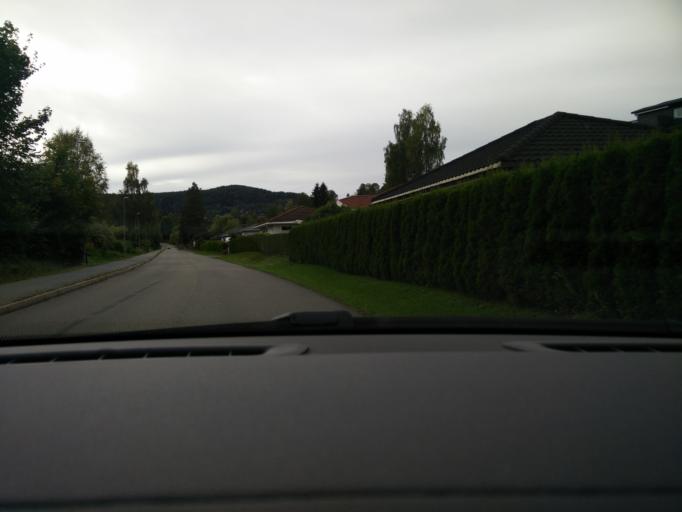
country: NO
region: Akershus
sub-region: Asker
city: Blakstad
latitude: 59.8234
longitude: 10.4534
